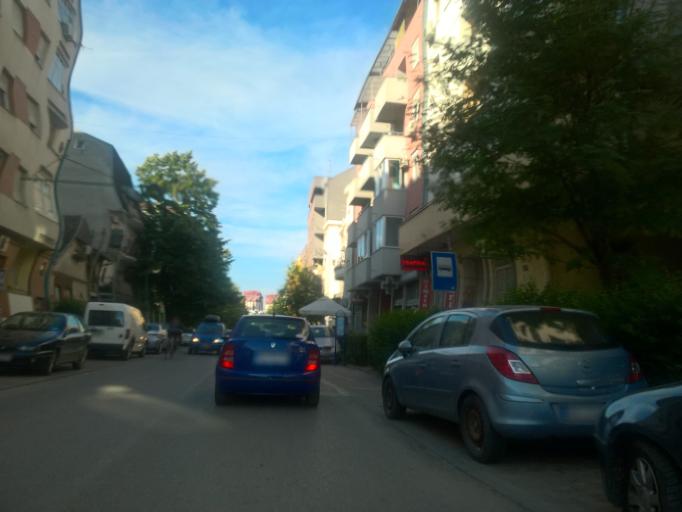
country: RS
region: Autonomna Pokrajina Vojvodina
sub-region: Juznobacki Okrug
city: Novi Sad
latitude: 45.2451
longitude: 19.8318
